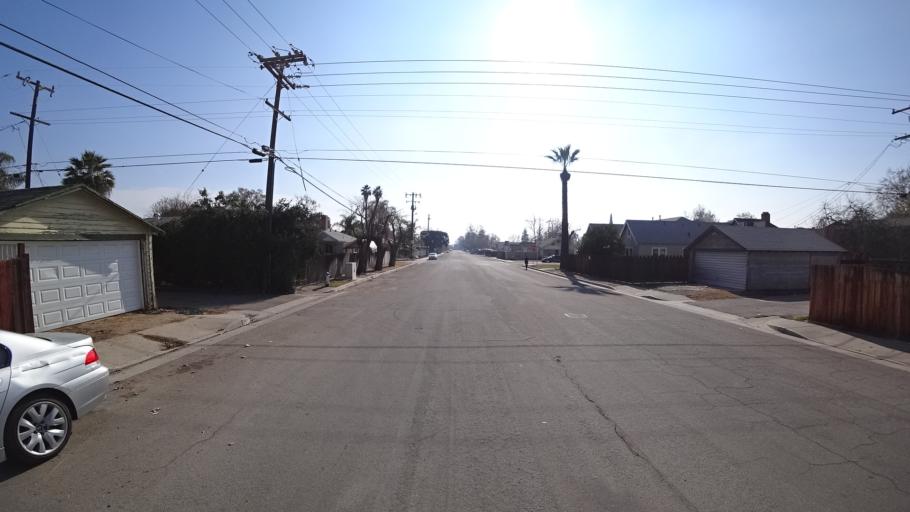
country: US
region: California
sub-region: Kern County
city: Bakersfield
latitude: 35.3881
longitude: -118.9991
